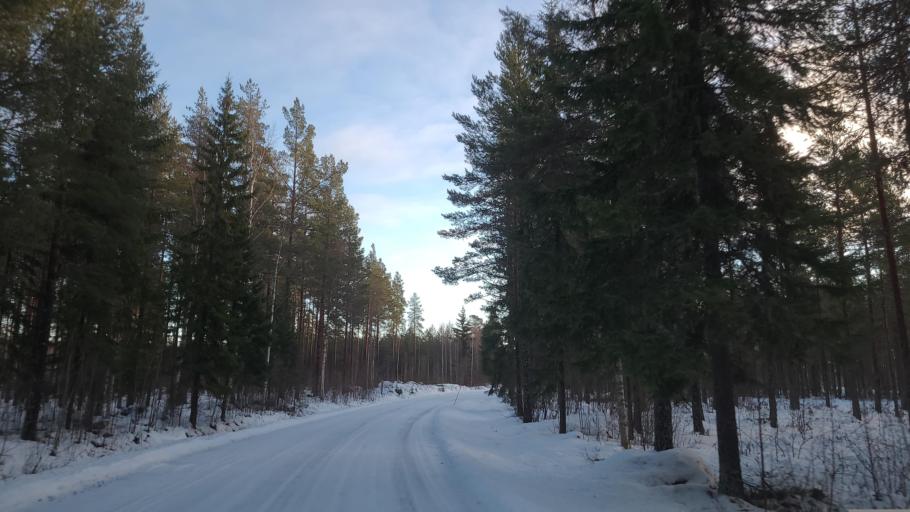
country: SE
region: Gaevleborg
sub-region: Bollnas Kommun
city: Kilafors
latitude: 61.4013
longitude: 16.6462
